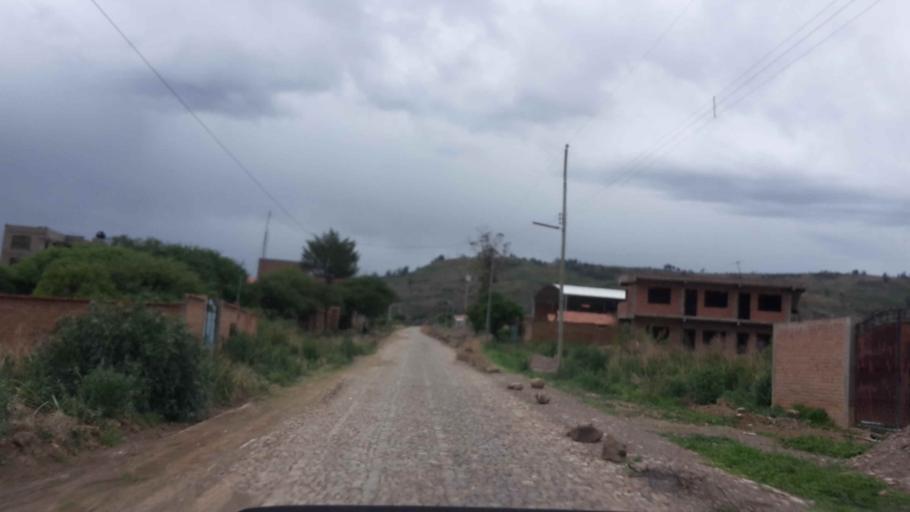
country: BO
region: Cochabamba
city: Cochabamba
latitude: -17.5383
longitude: -66.2009
